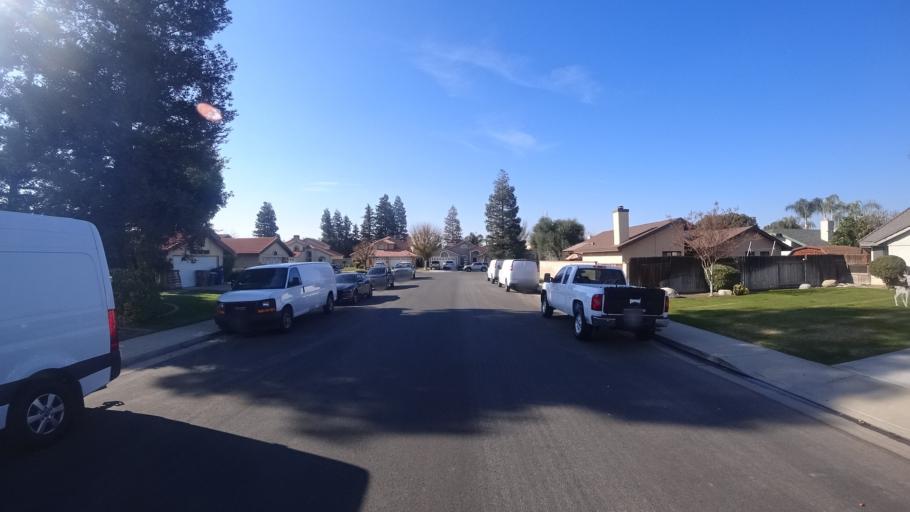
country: US
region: California
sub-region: Kern County
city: Greenacres
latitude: 35.3223
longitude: -119.1146
